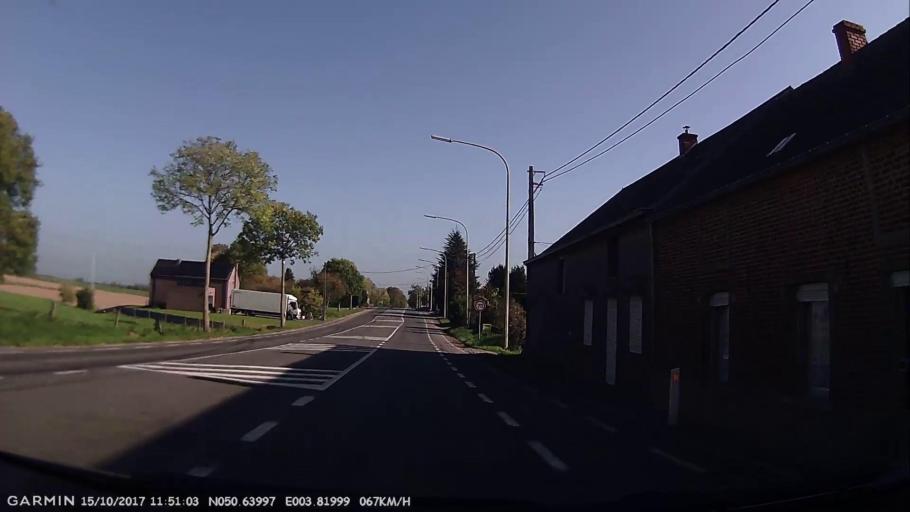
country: BE
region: Wallonia
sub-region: Province du Hainaut
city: Ath
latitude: 50.6400
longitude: 3.8201
